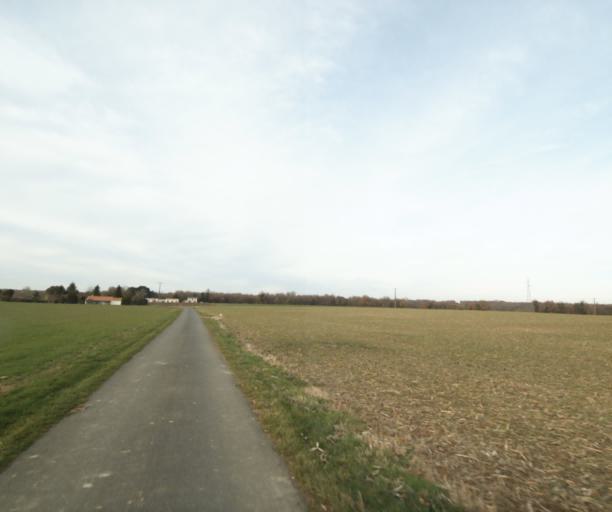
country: FR
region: Poitou-Charentes
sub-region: Departement de la Charente-Maritime
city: Saint-Hilaire-de-Villefranche
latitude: 45.8334
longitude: -0.5808
